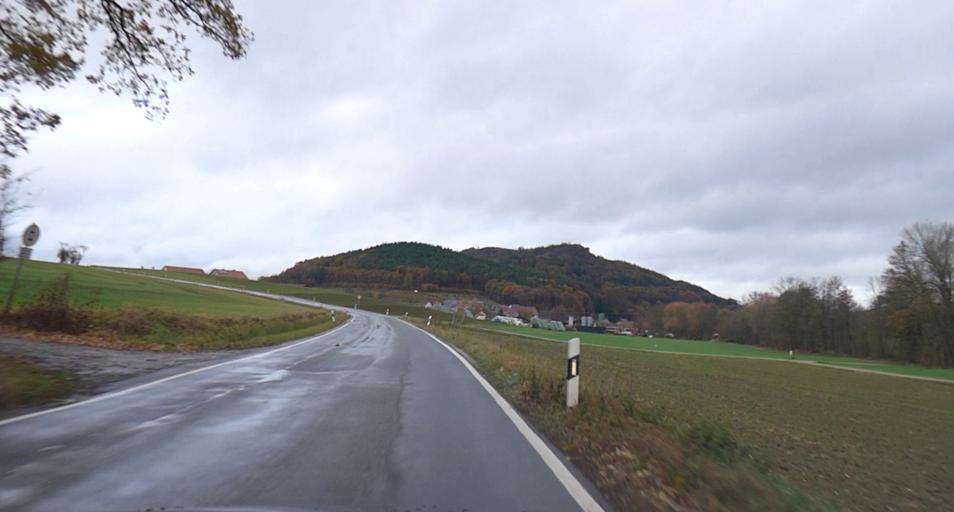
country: DE
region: Bavaria
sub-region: Upper Franconia
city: Leutenbach
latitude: 49.6950
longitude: 11.1656
